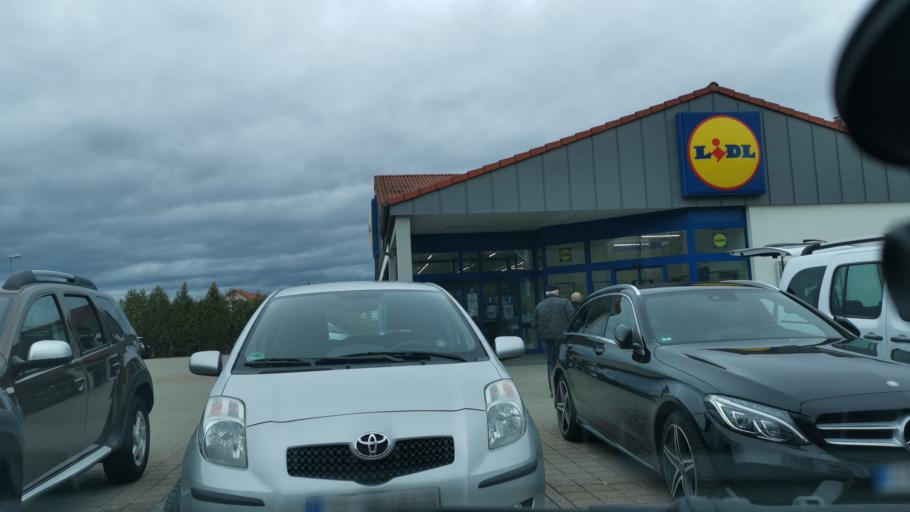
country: DE
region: Baden-Wuerttemberg
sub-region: Regierungsbezirk Stuttgart
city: Schwieberdingen
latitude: 48.8726
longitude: 9.0867
